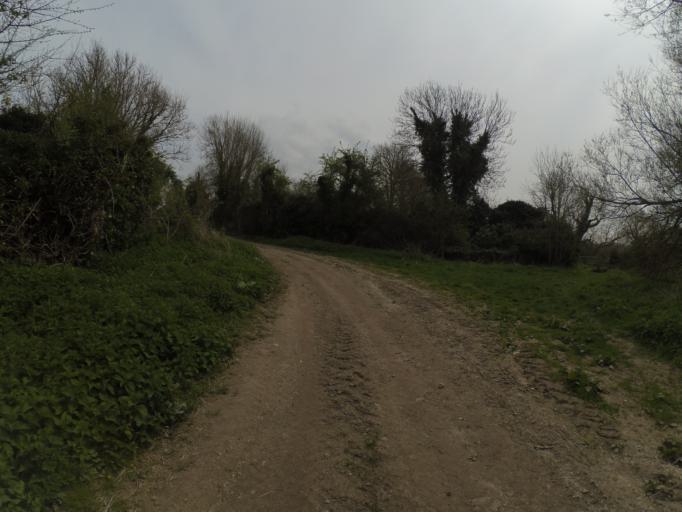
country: GB
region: England
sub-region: West Sussex
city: Arundel
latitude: 50.8734
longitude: -0.5312
